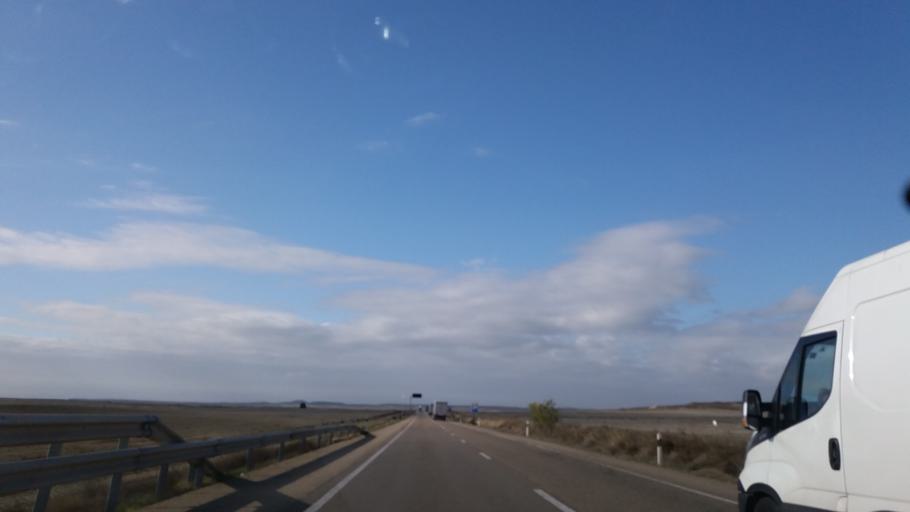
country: ES
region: Aragon
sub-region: Provincia de Huesca
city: Castejon de Monegros
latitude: 41.4971
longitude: -0.3265
